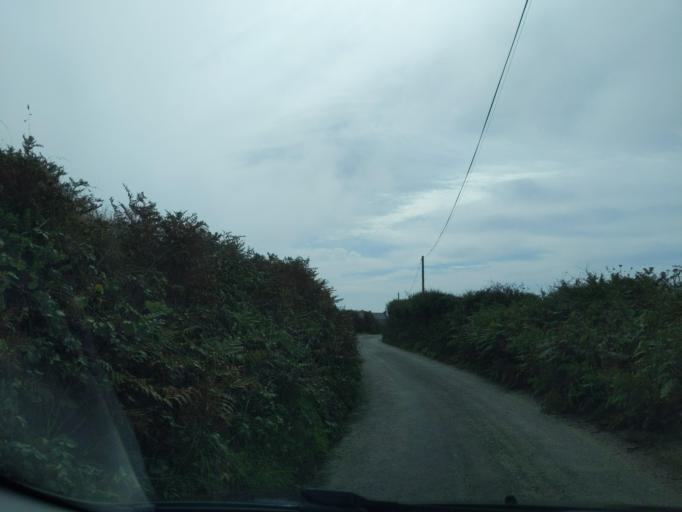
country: GB
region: England
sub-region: Cornwall
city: Germoe
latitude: 50.0993
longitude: -5.3638
